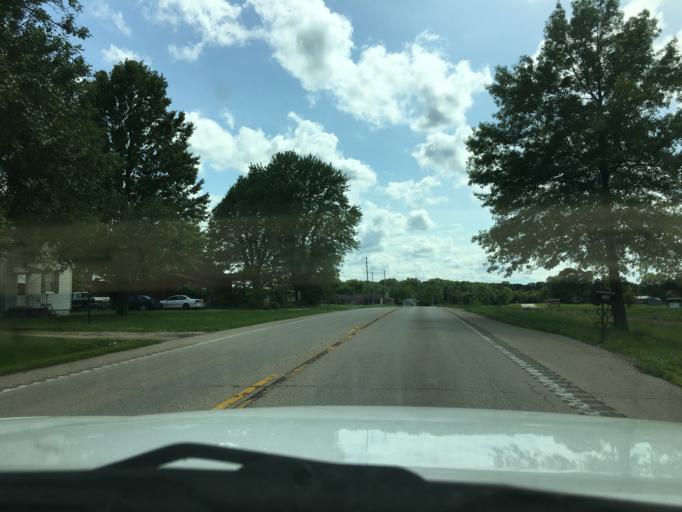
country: US
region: Missouri
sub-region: Franklin County
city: Gerald
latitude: 38.3967
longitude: -91.3383
